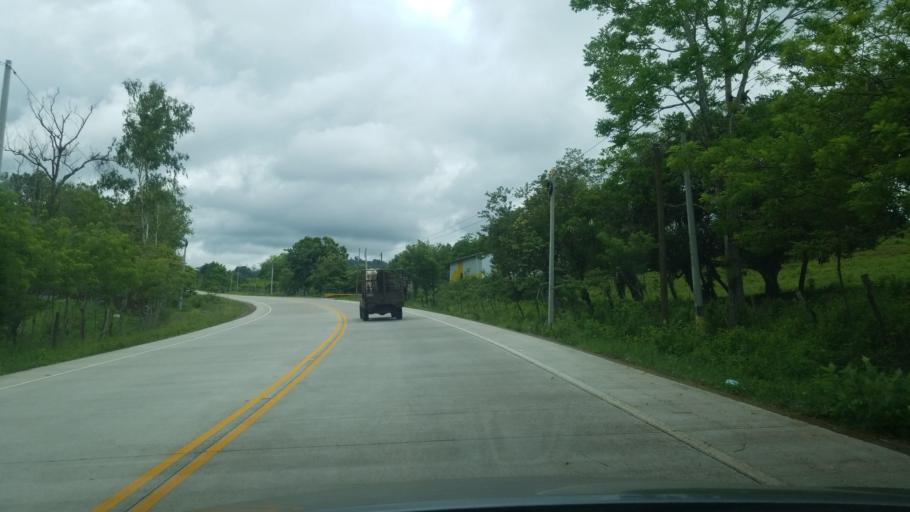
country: HN
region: Copan
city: San Jeronimo
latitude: 14.9811
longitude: -88.8789
